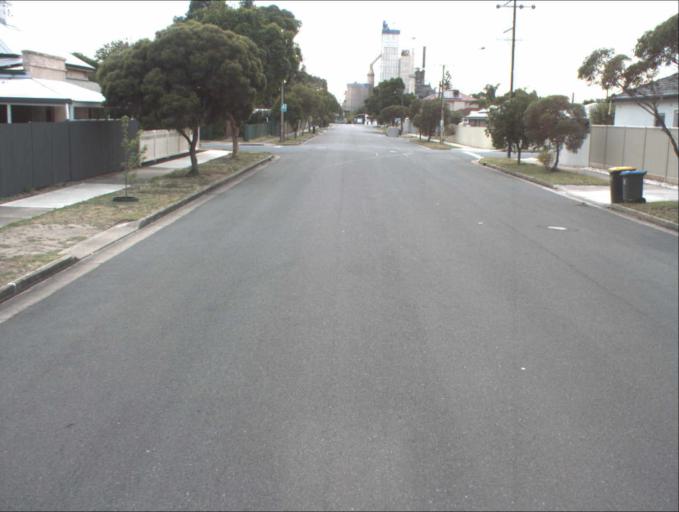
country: AU
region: South Australia
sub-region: Port Adelaide Enfield
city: Birkenhead
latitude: -34.8320
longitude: 138.4938
